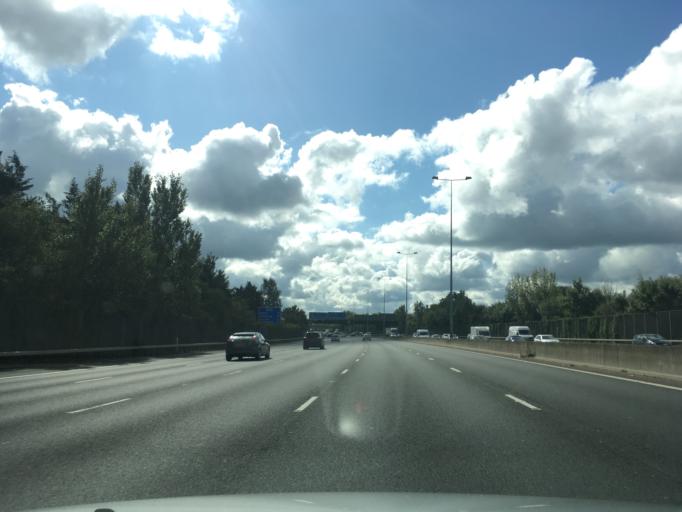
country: GB
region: England
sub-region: Surrey
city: Egham
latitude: 51.4288
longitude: -0.5408
